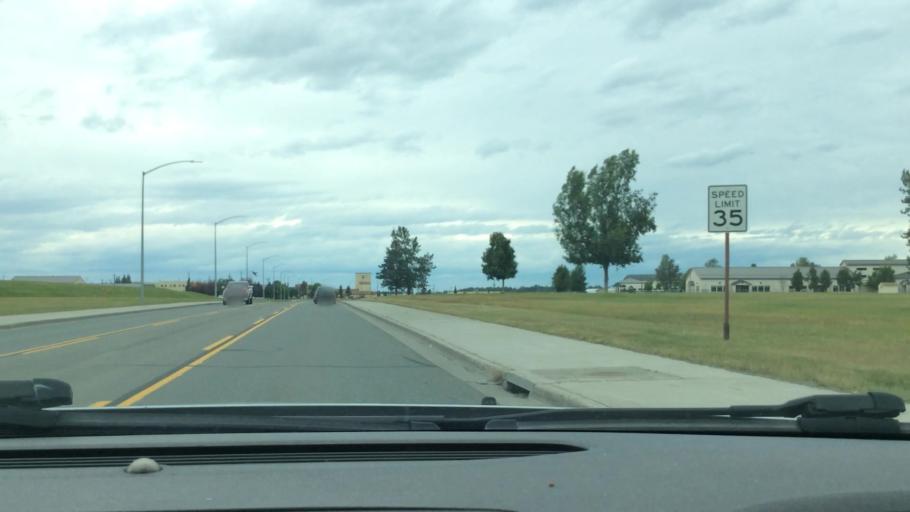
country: US
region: Alaska
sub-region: Anchorage Municipality
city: Anchorage
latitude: 61.2379
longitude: -149.8211
